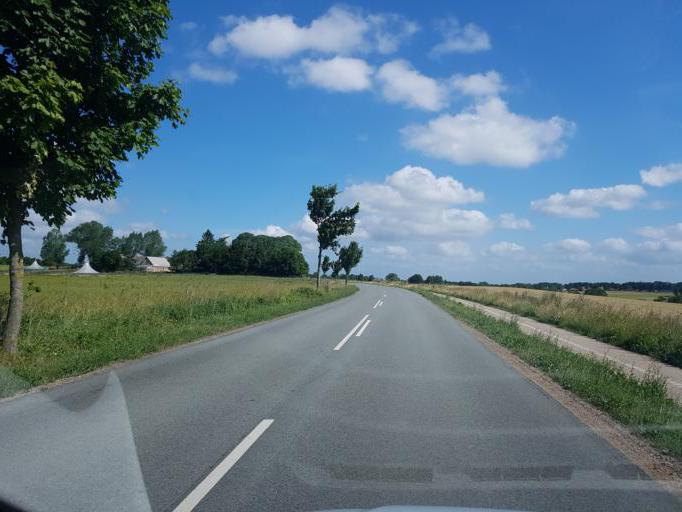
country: DK
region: Zealand
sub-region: Lejre Kommune
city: Lejre
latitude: 55.5868
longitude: 11.9692
